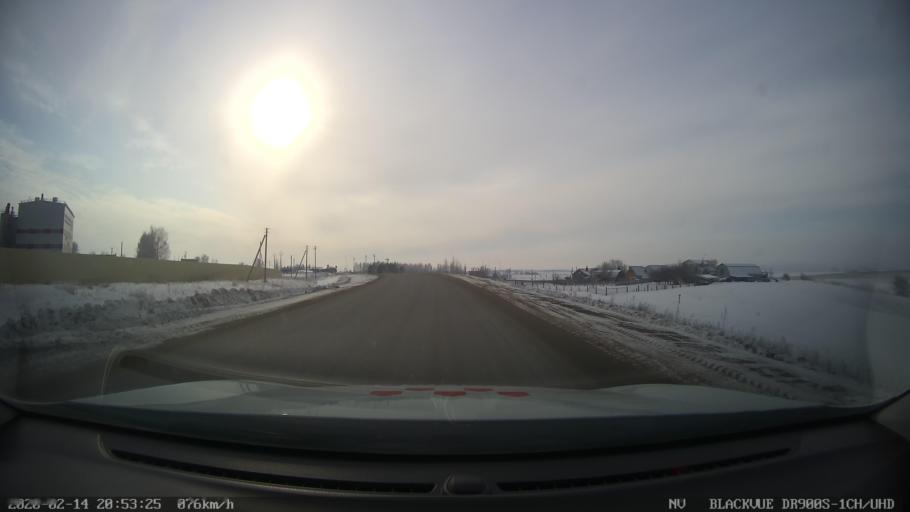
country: RU
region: Tatarstan
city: Kuybyshevskiy Zaton
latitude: 55.1948
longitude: 49.2472
